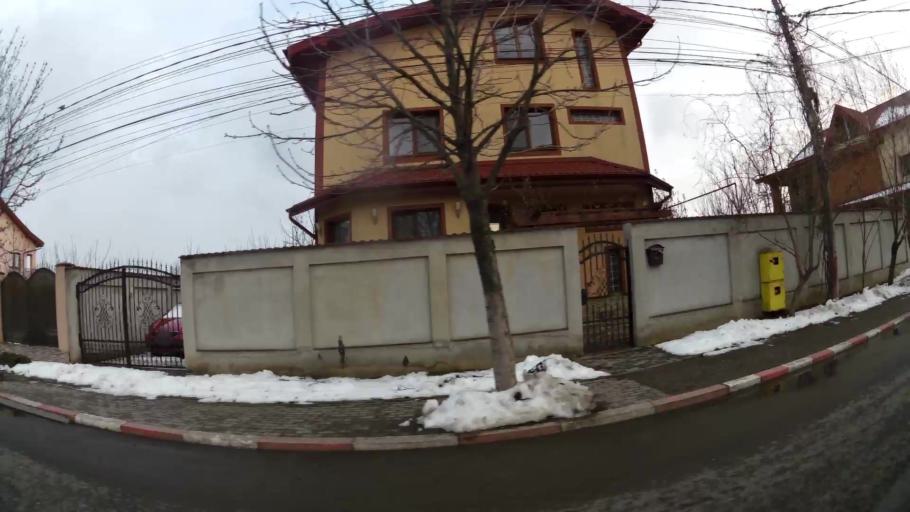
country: RO
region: Ilfov
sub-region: Voluntari City
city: Voluntari
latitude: 44.4961
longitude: 26.1677
